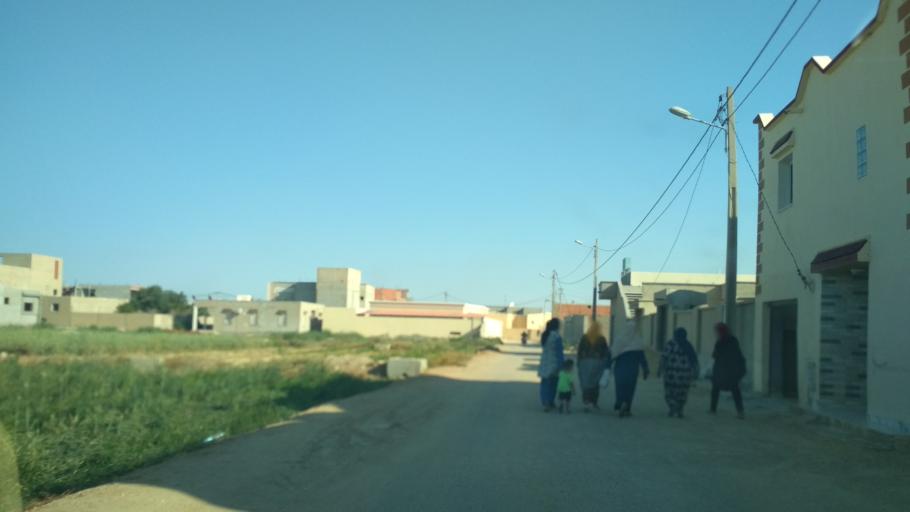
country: TN
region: Qabis
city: Gabes
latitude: 33.9506
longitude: 10.0638
